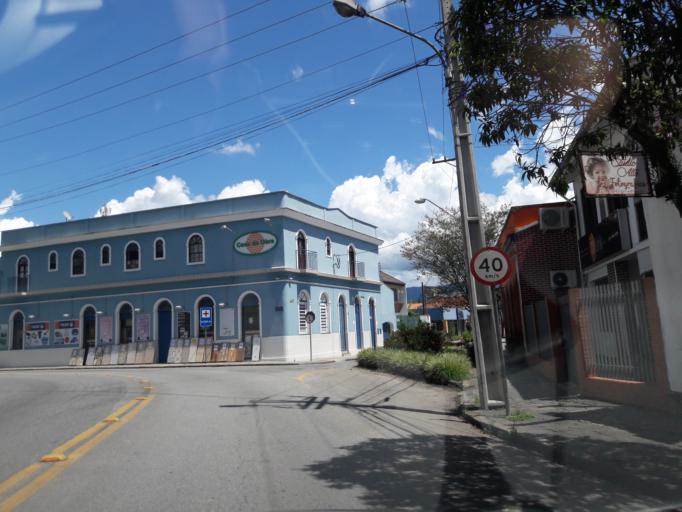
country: BR
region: Parana
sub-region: Antonina
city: Antonina
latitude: -25.4782
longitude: -48.8303
